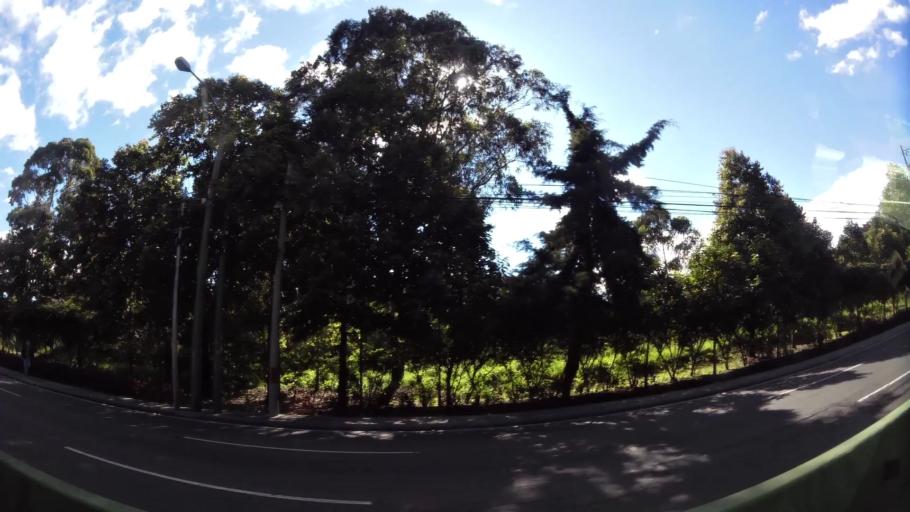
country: GT
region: Guatemala
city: Guatemala City
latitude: 14.6101
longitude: -90.5038
